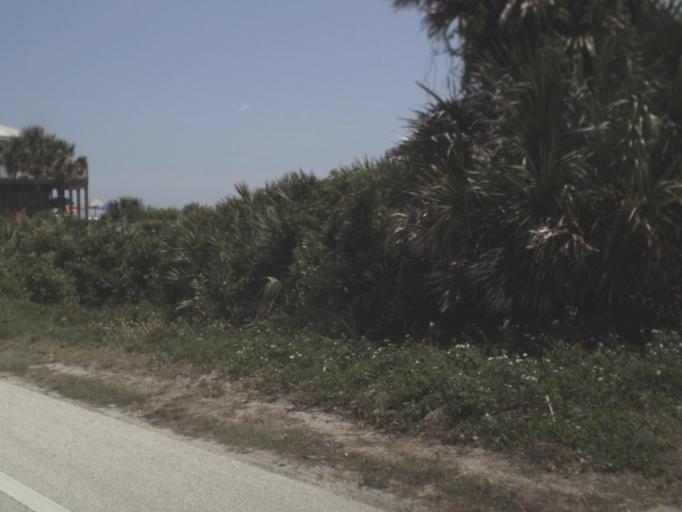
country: US
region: Florida
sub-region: Saint Johns County
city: Villano Beach
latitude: 29.9505
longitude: -81.3040
